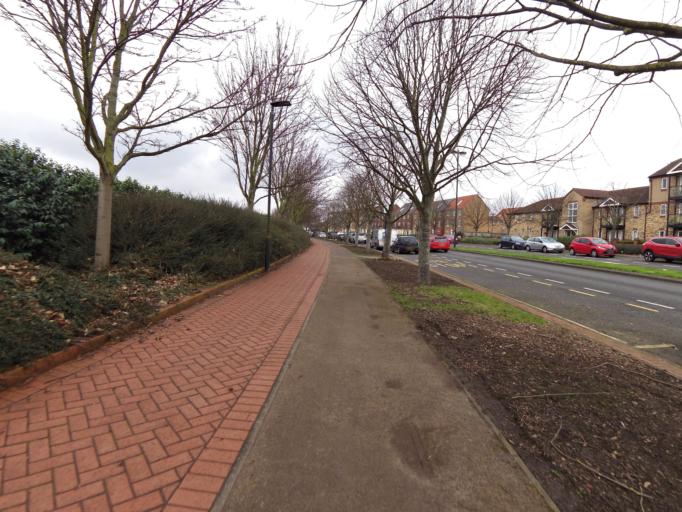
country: GB
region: England
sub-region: Doncaster
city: Doncaster
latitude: 53.5094
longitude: -1.1019
